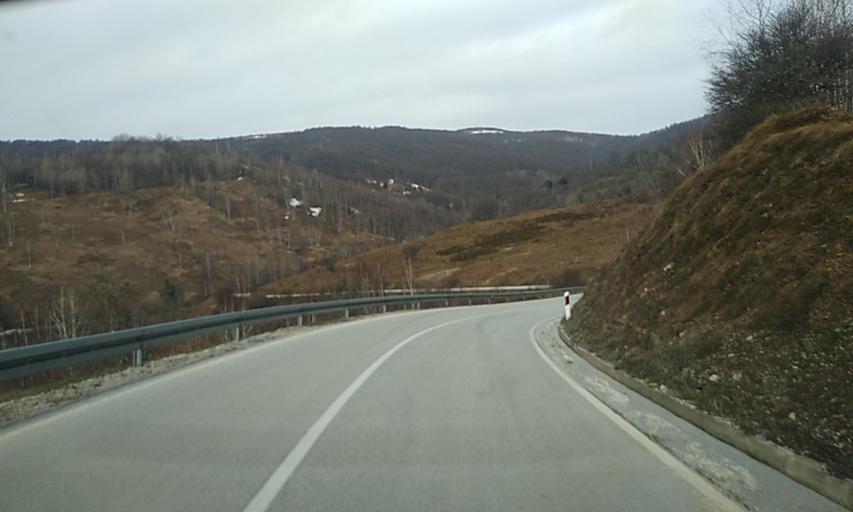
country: RS
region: Central Serbia
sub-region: Pcinjski Okrug
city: Bosilegrad
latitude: 42.6426
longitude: 22.3791
